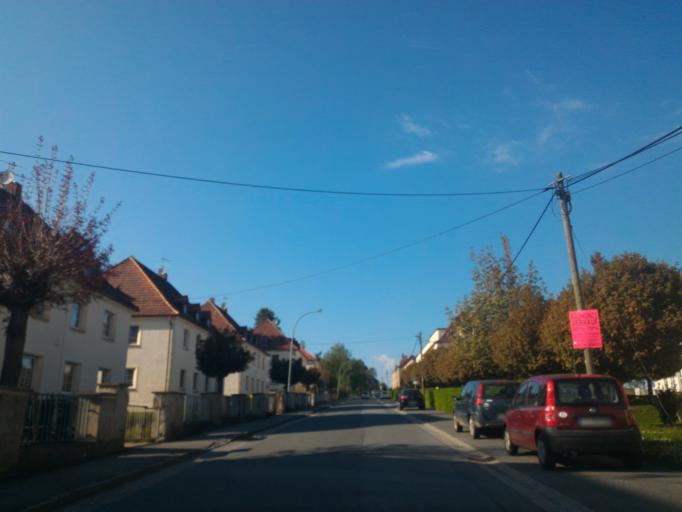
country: DE
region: Saxony
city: Seifhennersdorf
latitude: 50.9367
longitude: 14.6077
